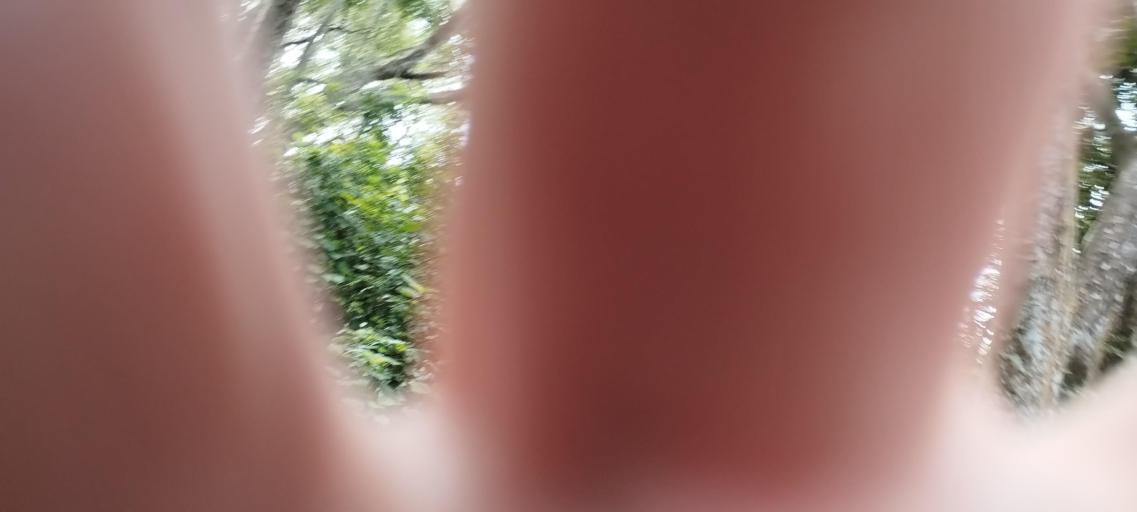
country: NP
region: Far Western
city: Tikapur
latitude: 28.4847
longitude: 81.2501
